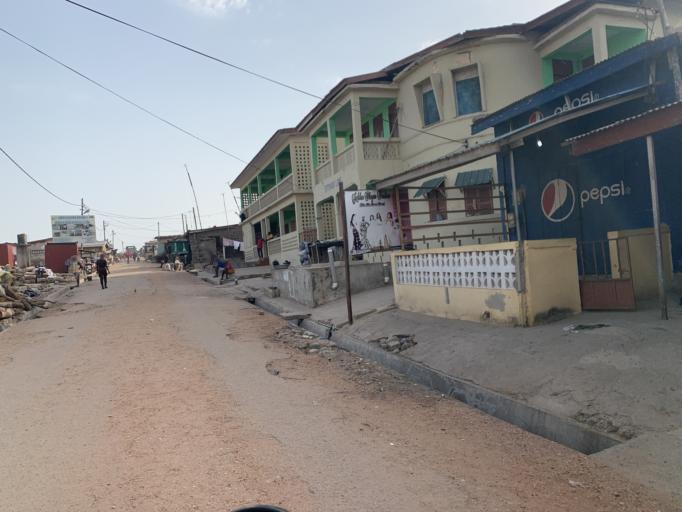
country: GH
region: Central
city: Winneba
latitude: 5.3377
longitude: -0.6190
